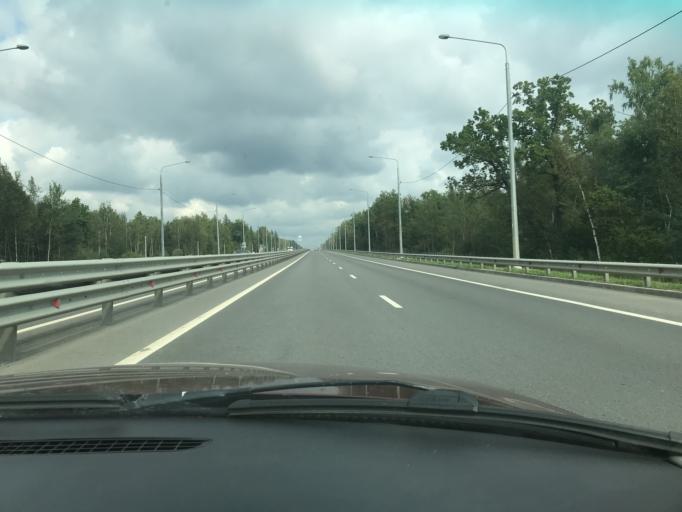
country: RU
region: Kaluga
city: Mstikhino
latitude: 54.6465
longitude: 36.1355
